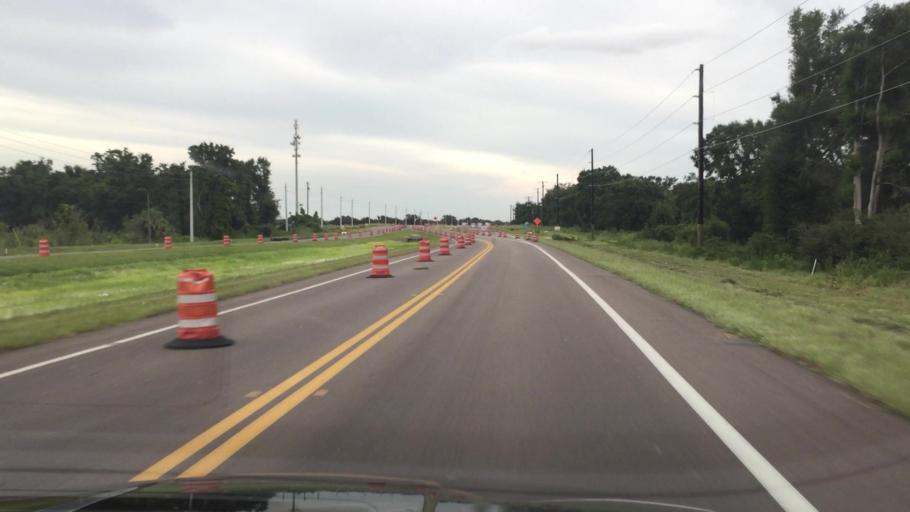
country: US
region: Florida
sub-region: DeSoto County
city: Arcadia
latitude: 27.3484
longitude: -81.8025
